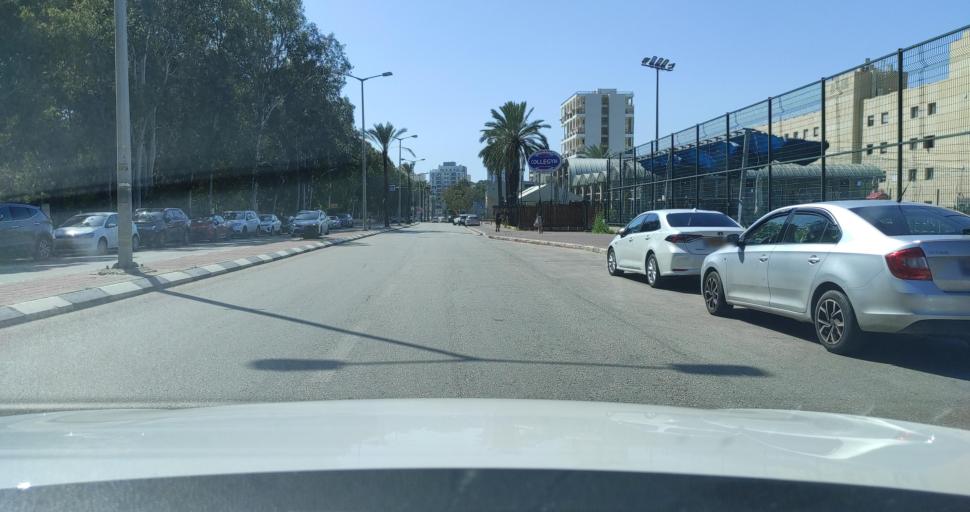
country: IL
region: Central District
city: Nordiyya
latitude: 32.3069
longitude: 34.8790
